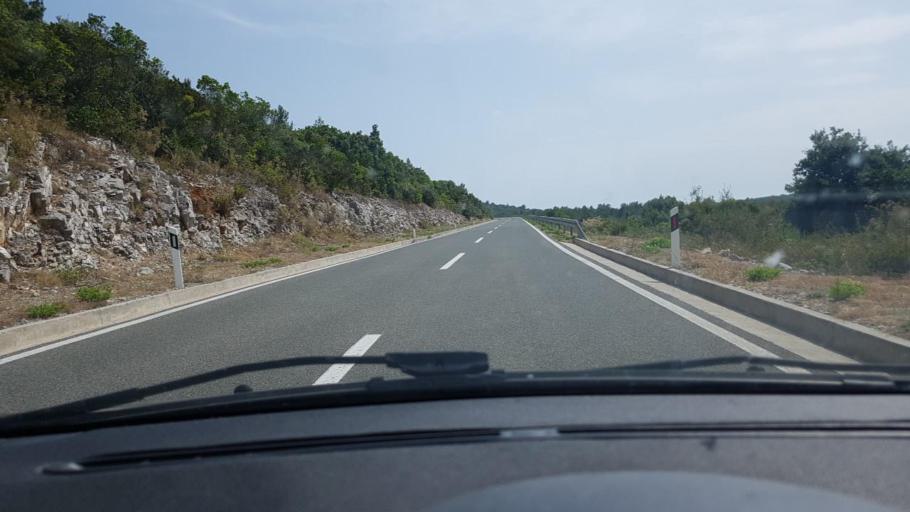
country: HR
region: Dubrovacko-Neretvanska
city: Smokvica
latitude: 42.9536
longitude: 16.9429
